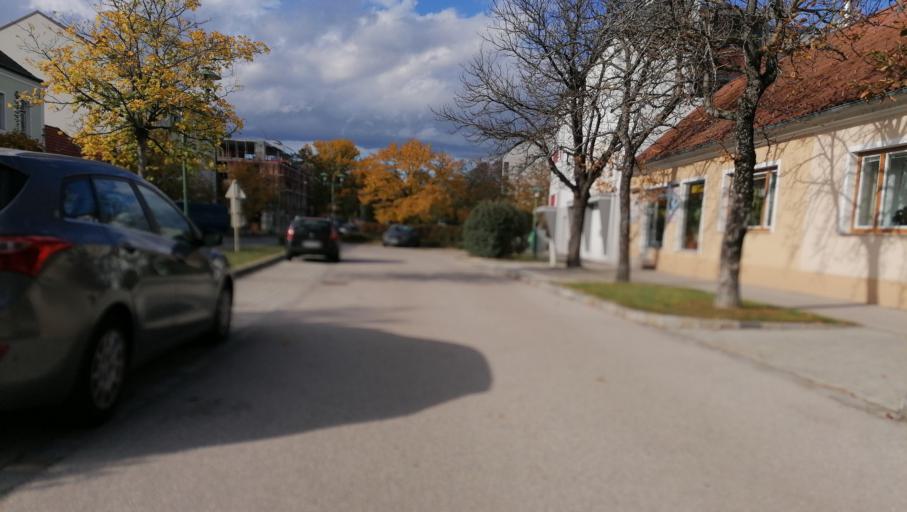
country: AT
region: Lower Austria
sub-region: Politischer Bezirk Baden
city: Tattendorf
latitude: 47.9559
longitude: 16.3028
